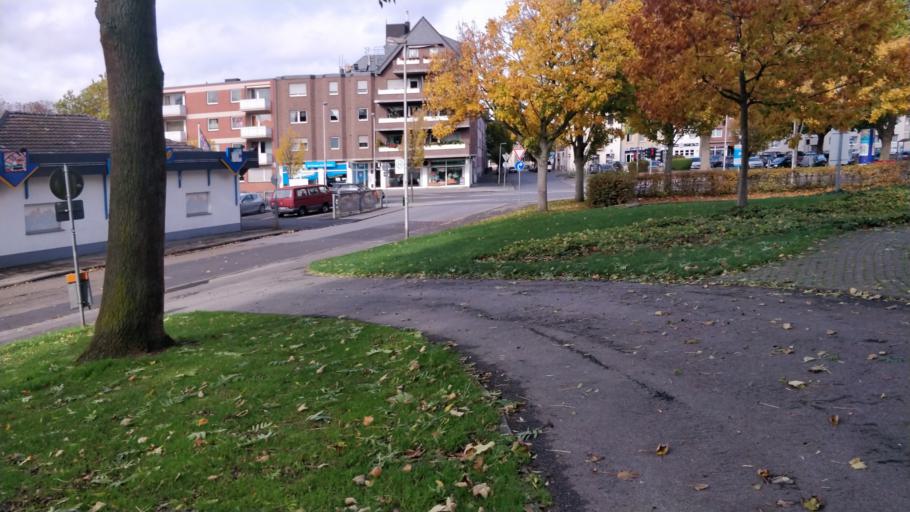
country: DE
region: North Rhine-Westphalia
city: Julich
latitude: 50.9196
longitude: 6.3549
